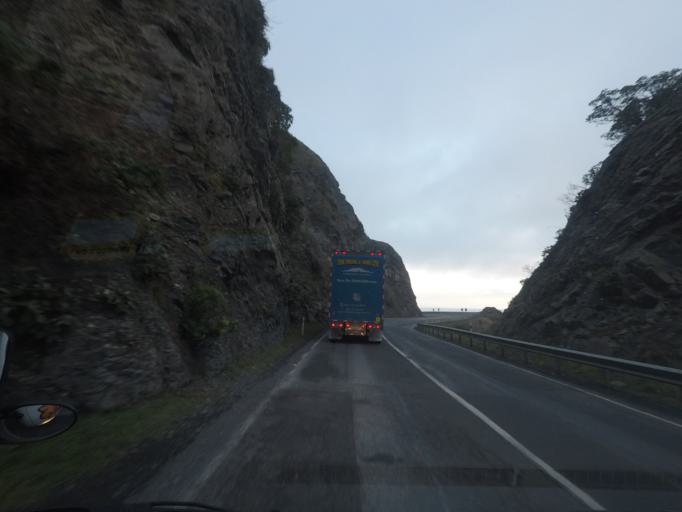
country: NZ
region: Canterbury
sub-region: Kaikoura District
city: Kaikoura
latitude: -42.4497
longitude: 173.5751
